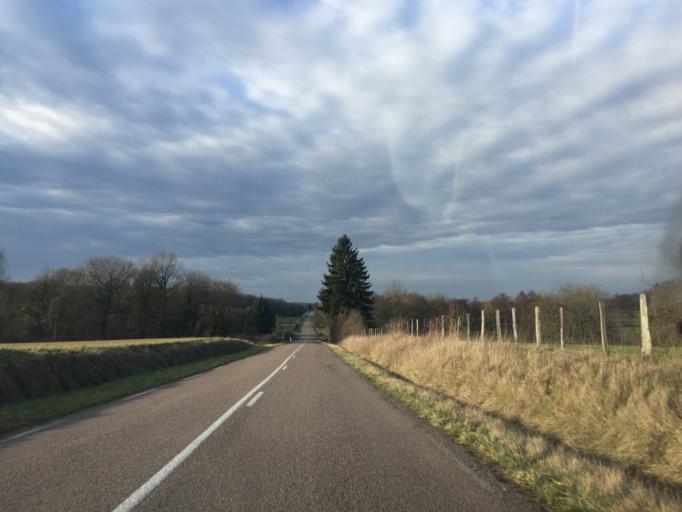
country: FR
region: Franche-Comte
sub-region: Departement du Jura
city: Arbois
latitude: 46.9263
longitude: 5.6898
